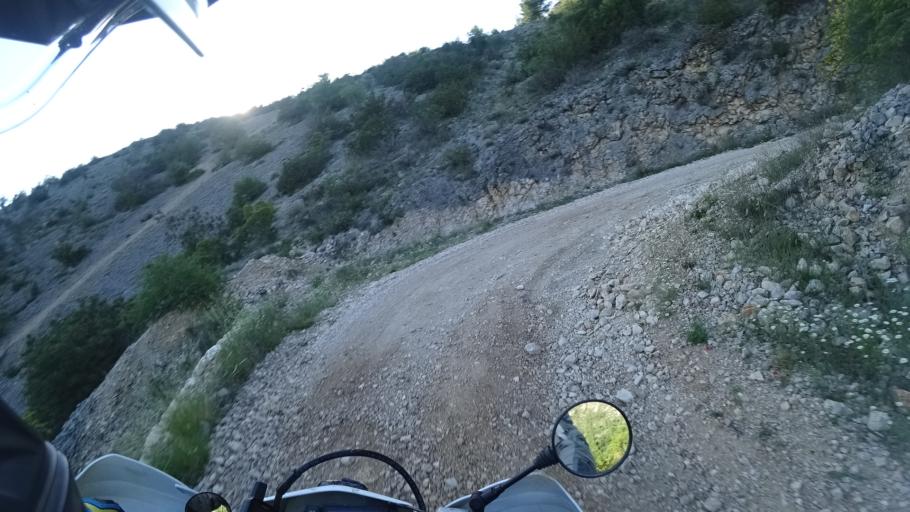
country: HR
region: Sibensko-Kniniska
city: Drnis
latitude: 43.8285
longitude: 16.0216
